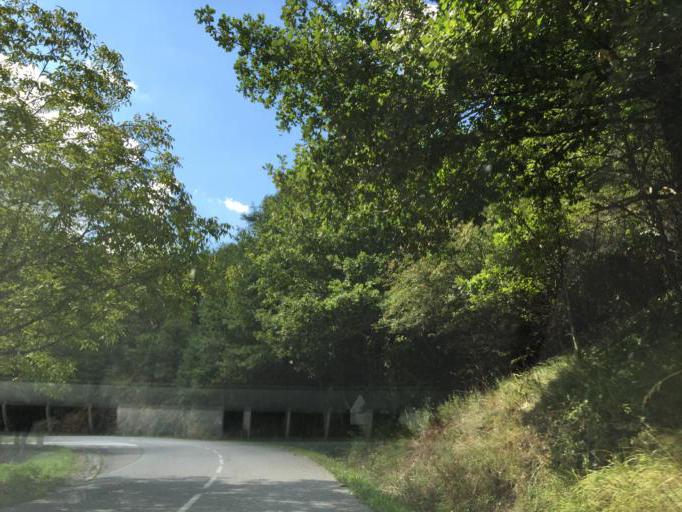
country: FR
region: Midi-Pyrenees
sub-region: Departement de l'Aveyron
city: Firmi
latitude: 44.5884
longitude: 2.3996
